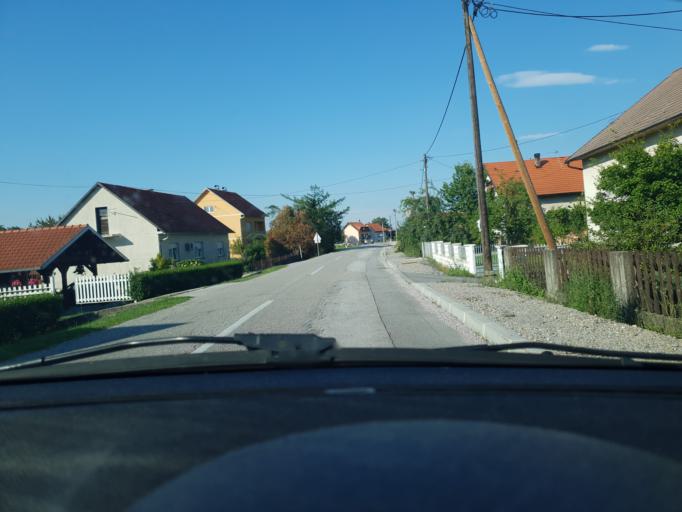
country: HR
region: Krapinsko-Zagorska
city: Oroslavje
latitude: 45.9854
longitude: 15.9122
